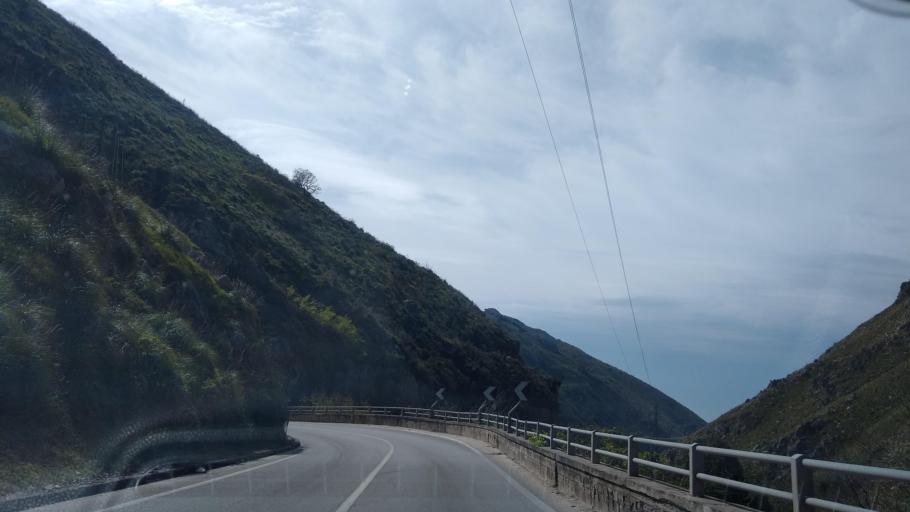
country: IT
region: Sicily
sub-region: Palermo
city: Pioppo
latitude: 38.0494
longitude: 13.1942
